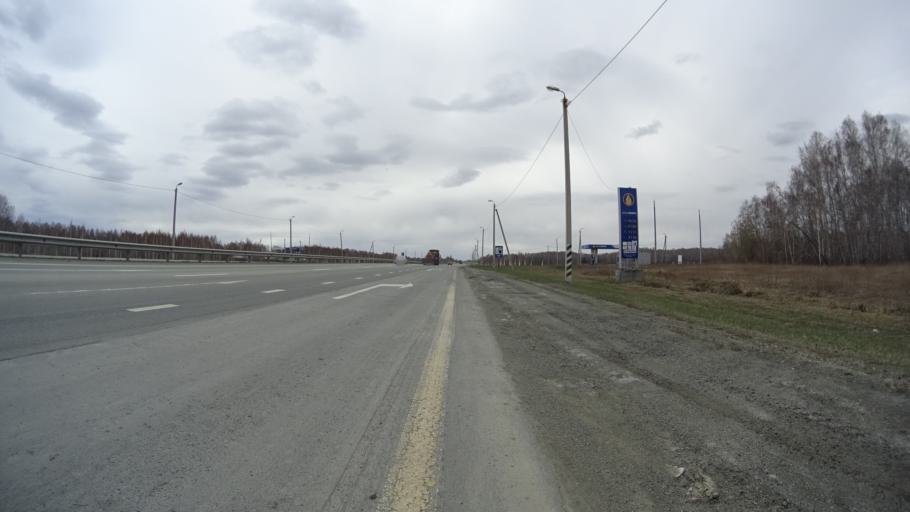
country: RU
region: Chelyabinsk
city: Yemanzhelinka
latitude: 54.8350
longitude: 61.3125
